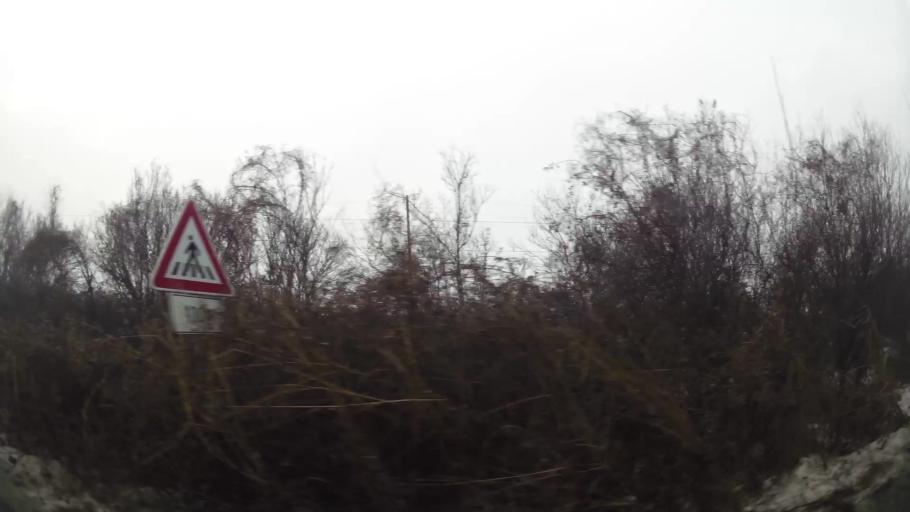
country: MK
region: Ilinden
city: Idrizovo
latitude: 41.9515
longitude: 21.5836
